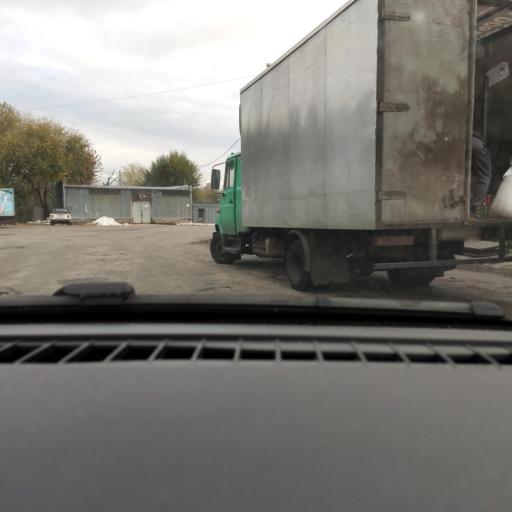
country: RU
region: Voronezj
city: Voronezh
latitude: 51.6582
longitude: 39.2700
